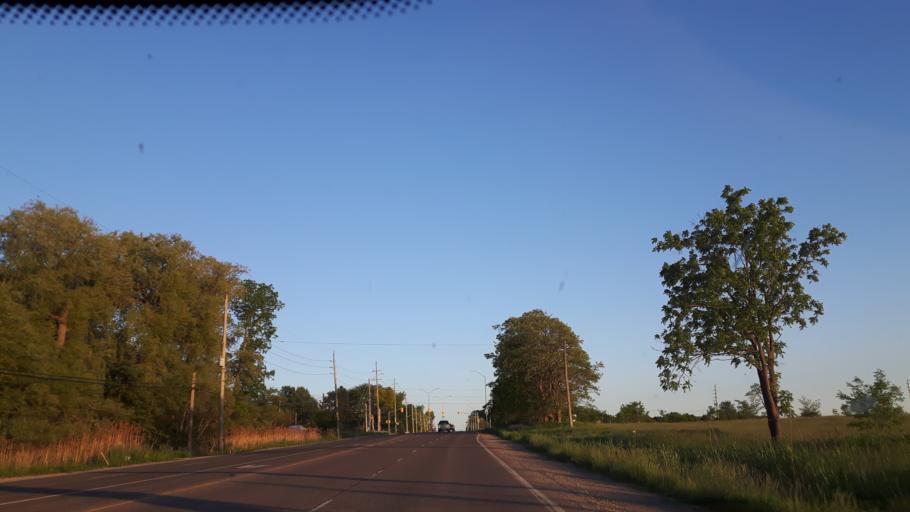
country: CA
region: Ontario
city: London
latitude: 43.0403
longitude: -81.2898
